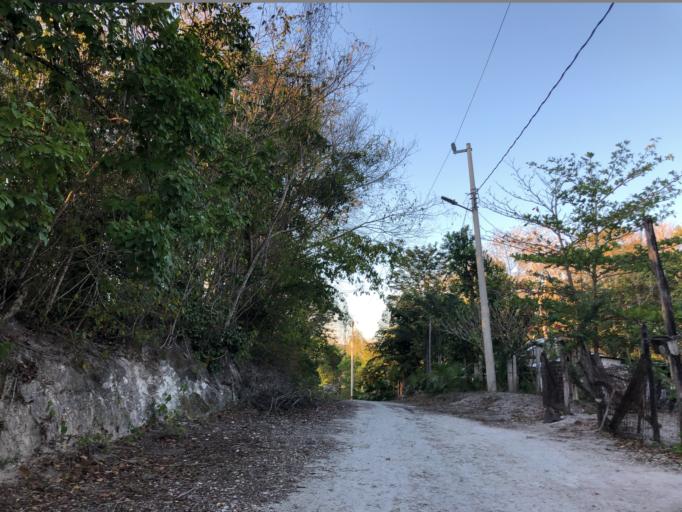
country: MX
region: Quintana Roo
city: Nicolas Bravo
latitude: 18.4498
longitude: -89.3057
